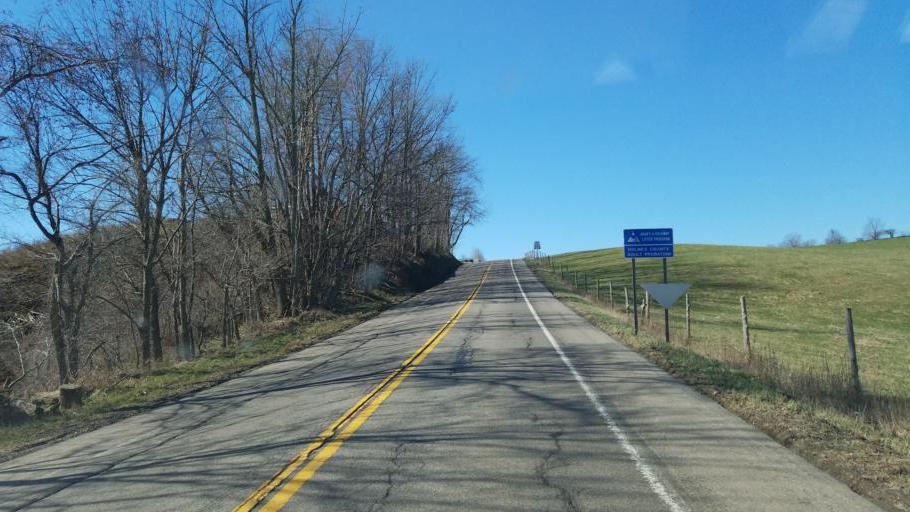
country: US
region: Ohio
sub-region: Wayne County
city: Apple Creek
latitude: 40.6679
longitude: -81.7403
